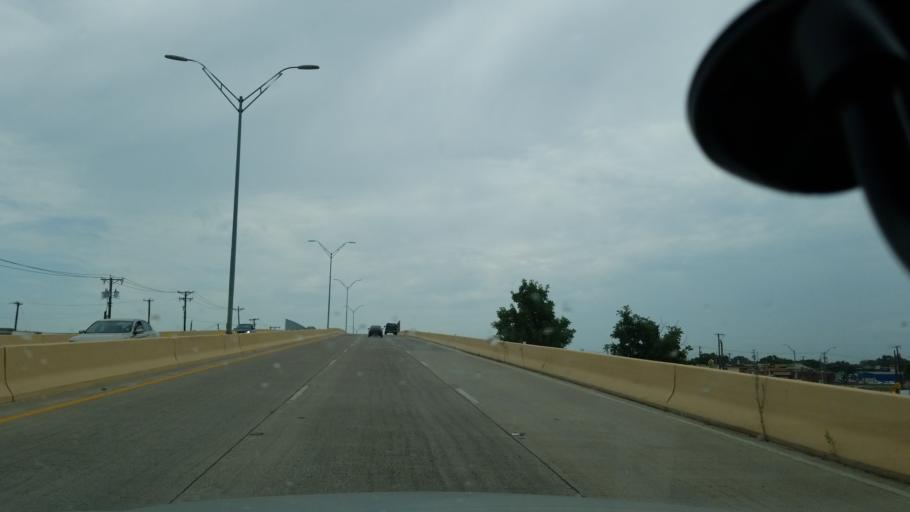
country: US
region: Texas
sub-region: Dallas County
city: Grand Prairie
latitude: 32.7435
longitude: -96.9944
